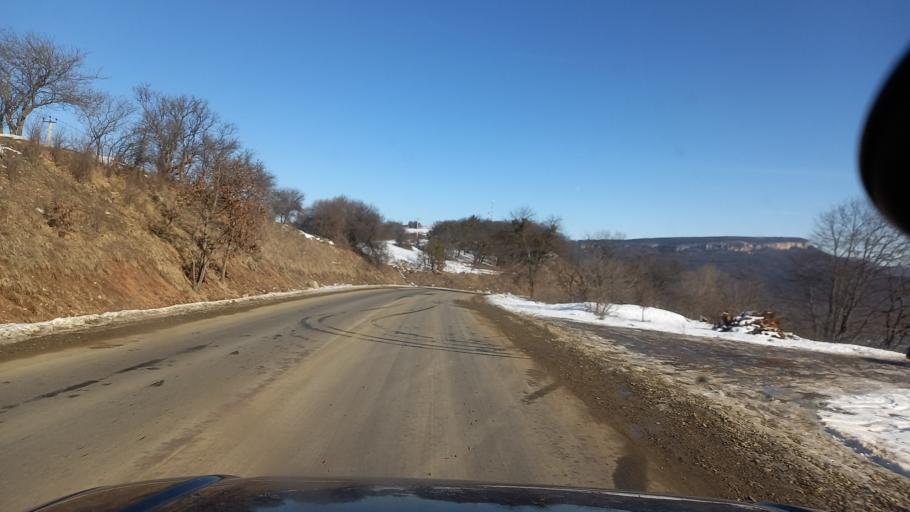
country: RU
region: Adygeya
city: Kamennomostskiy
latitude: 44.2362
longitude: 40.1531
